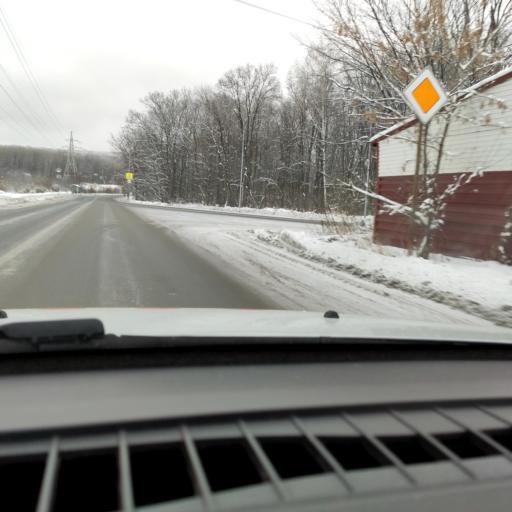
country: RU
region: Samara
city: Novosemeykino
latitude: 53.3475
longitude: 50.2379
